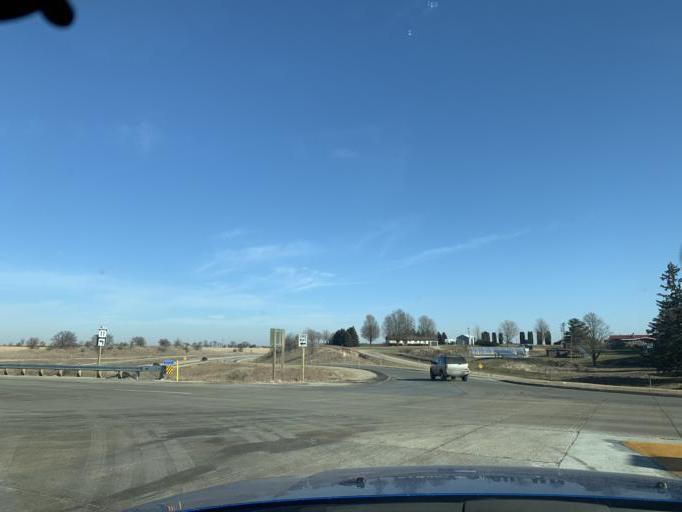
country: US
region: Wisconsin
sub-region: Green County
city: Monroe
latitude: 42.6128
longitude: -89.6525
